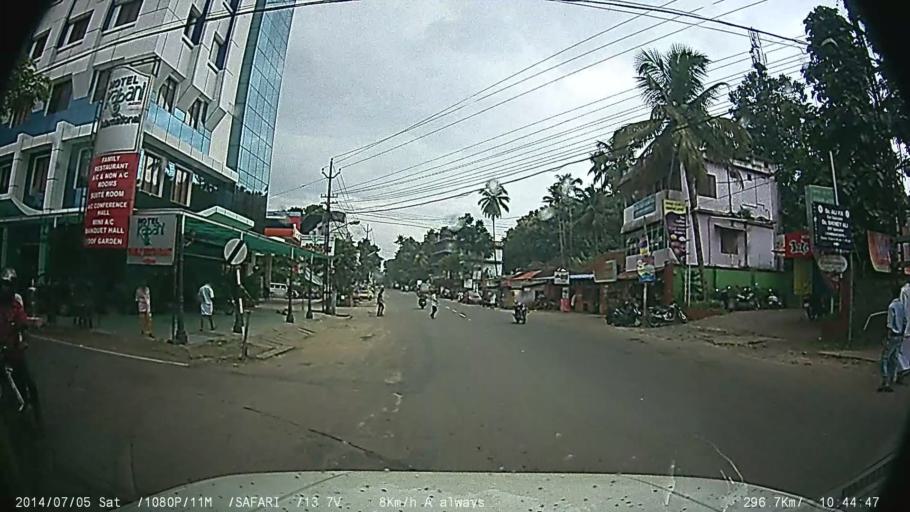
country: IN
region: Kerala
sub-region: Ernakulam
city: Muvattupula
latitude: 9.9793
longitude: 76.5861
